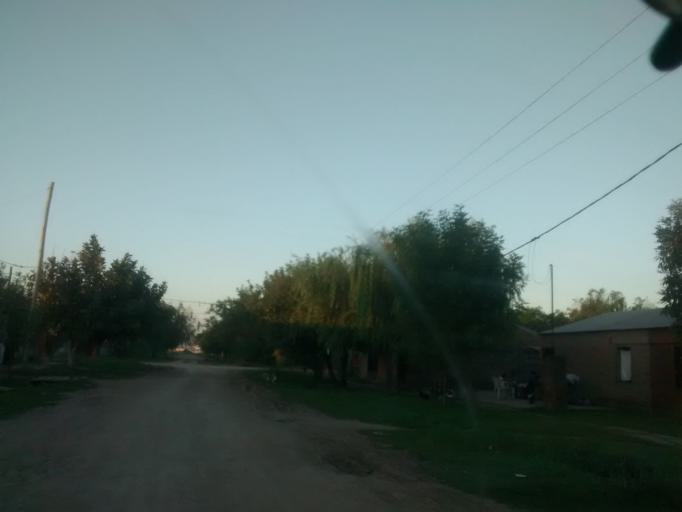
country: AR
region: Chaco
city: Fontana
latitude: -27.3998
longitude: -58.9920
